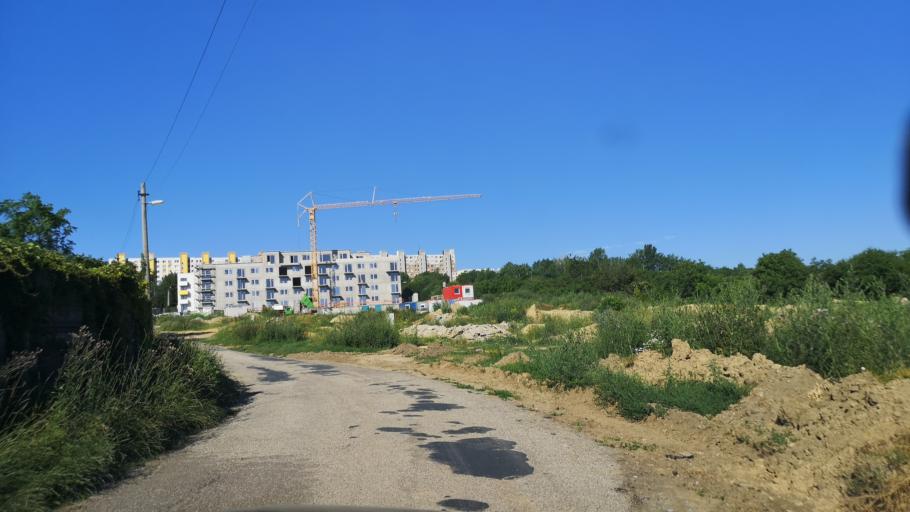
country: SK
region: Nitriansky
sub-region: Okres Nitra
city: Nitra
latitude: 48.3099
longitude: 18.0536
